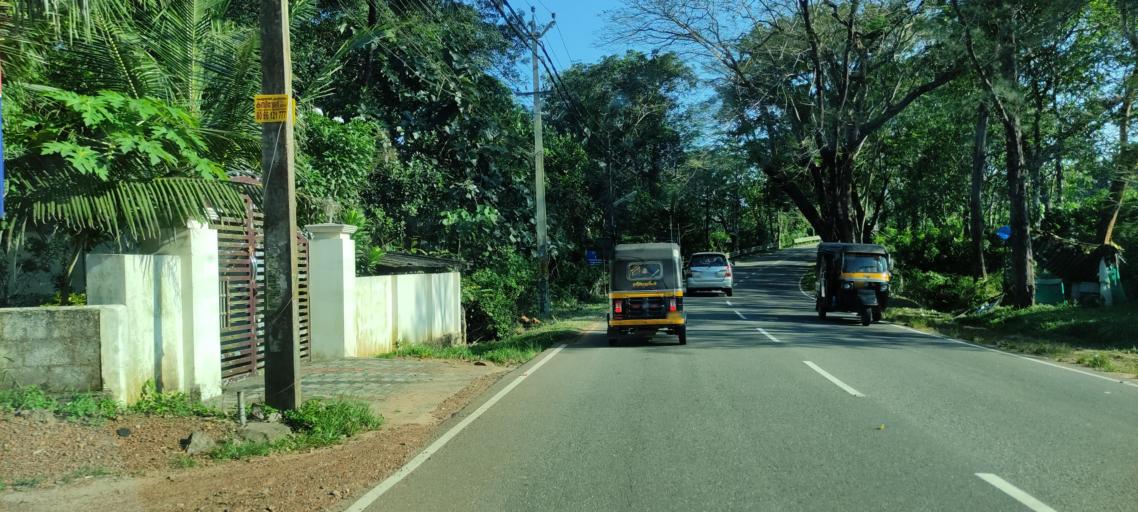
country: IN
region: Kerala
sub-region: Pattanamtitta
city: Adur
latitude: 9.1634
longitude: 76.7436
